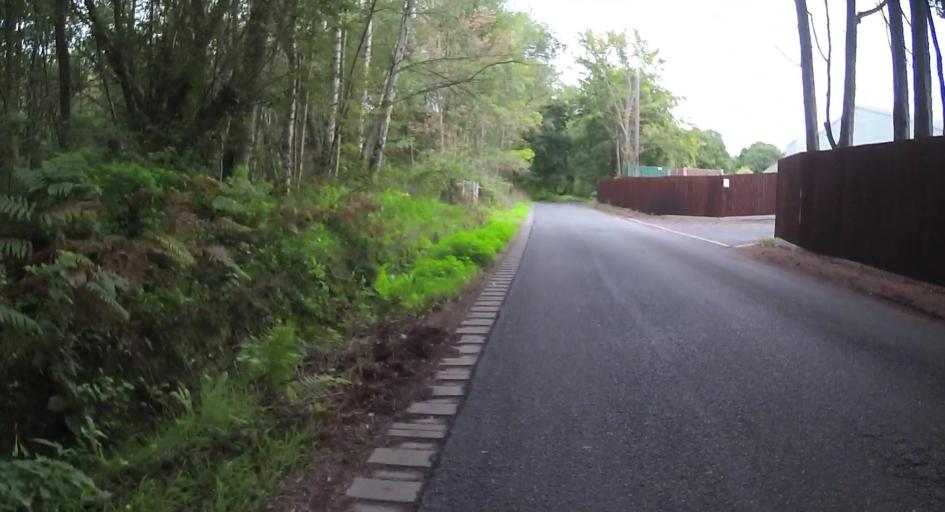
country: GB
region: England
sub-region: Surrey
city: West Byfleet
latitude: 51.3207
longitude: -0.4980
